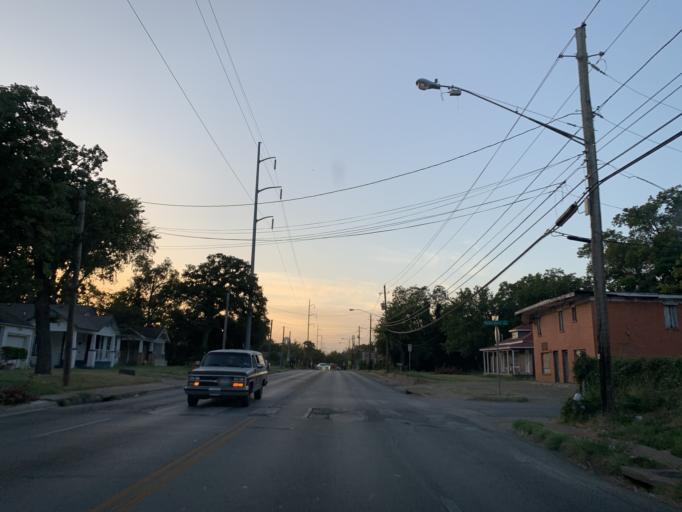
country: US
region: Texas
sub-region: Dallas County
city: Dallas
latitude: 32.7627
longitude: -96.7608
